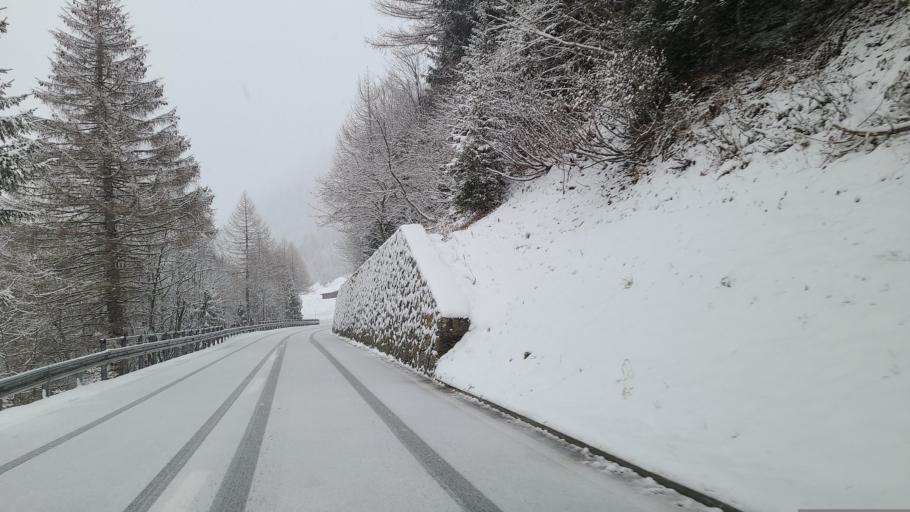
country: CH
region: Ticino
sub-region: Leventina District
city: Airolo
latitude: 46.5111
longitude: 8.5320
